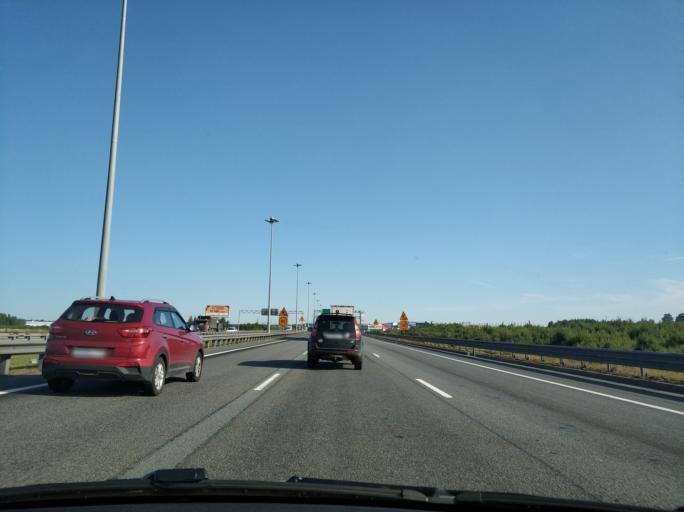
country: RU
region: Leningrad
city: Bugry
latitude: 60.0787
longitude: 30.3803
